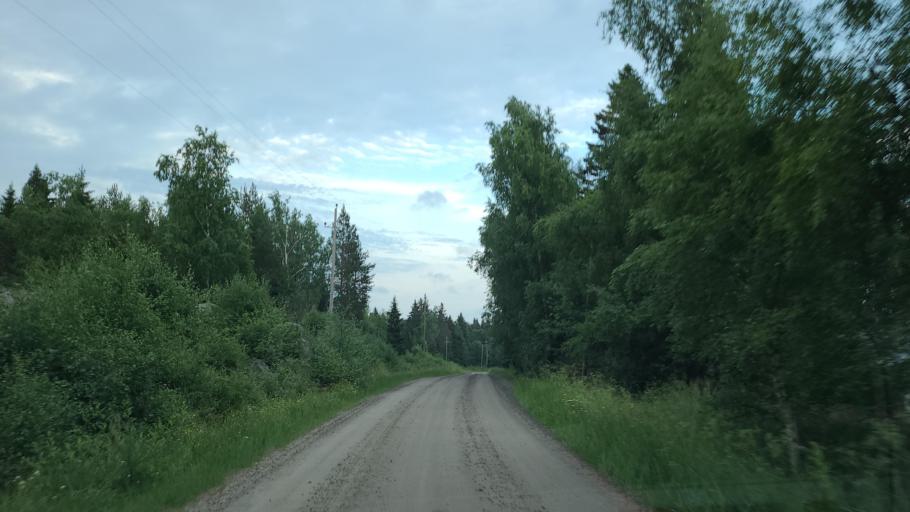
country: FI
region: Ostrobothnia
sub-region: Vaasa
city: Replot
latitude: 63.3157
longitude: 21.1578
